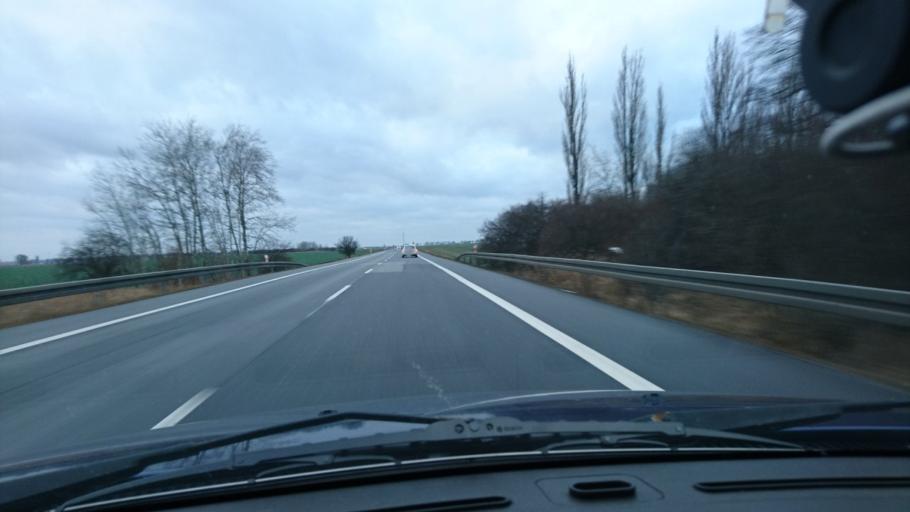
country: PL
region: Opole Voivodeship
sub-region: Powiat kluczborski
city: Kluczbork
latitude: 50.9849
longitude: 18.2407
